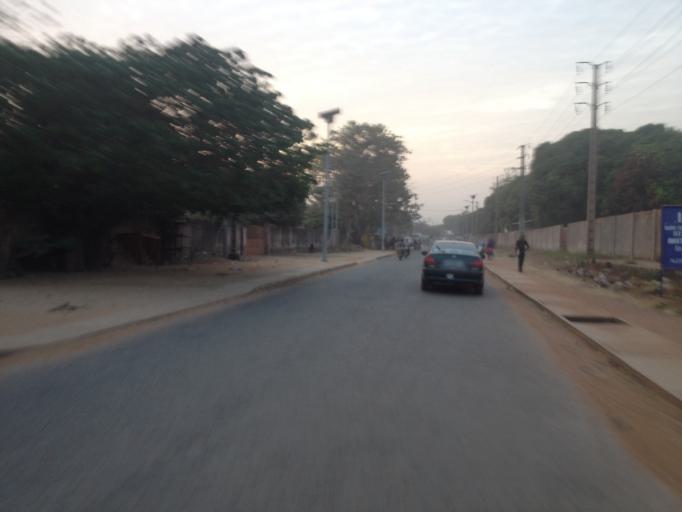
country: BJ
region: Borgou
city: Parakou
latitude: 9.3361
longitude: 2.6413
